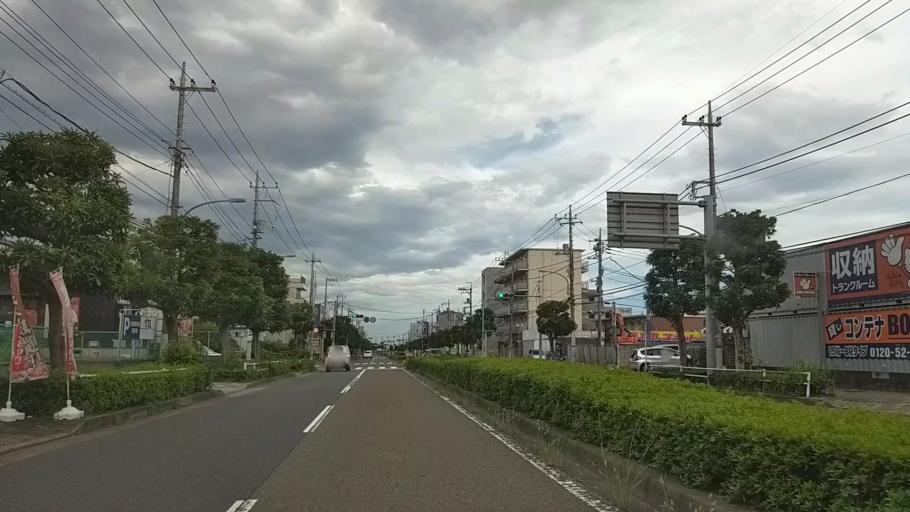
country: JP
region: Tokyo
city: Hachioji
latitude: 35.6385
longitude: 139.3098
